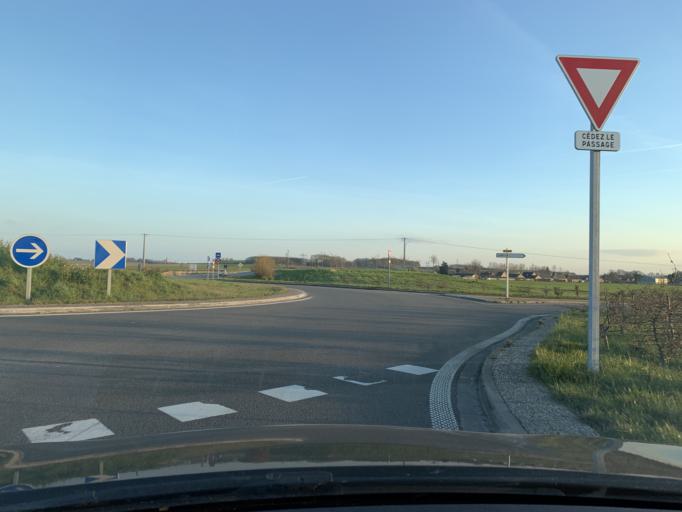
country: FR
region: Nord-Pas-de-Calais
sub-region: Departement du Nord
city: Cantin
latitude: 50.3172
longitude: 3.1326
